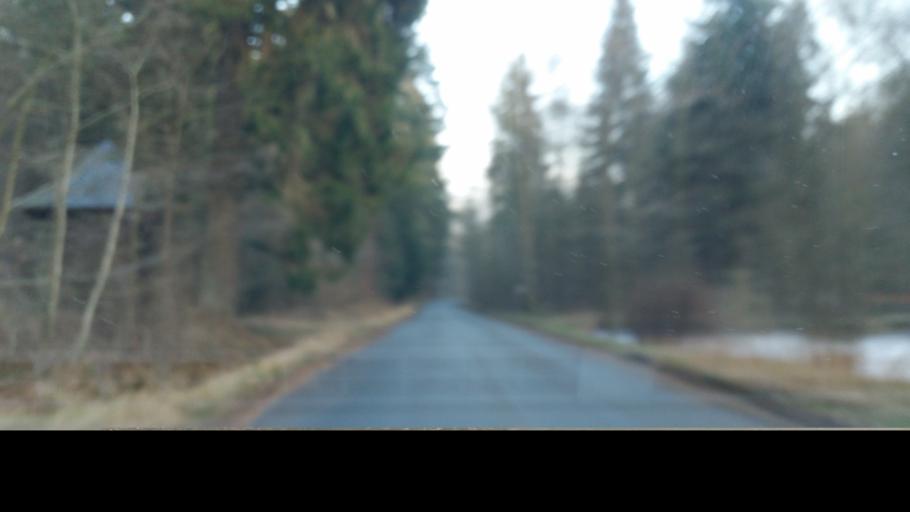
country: DE
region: Lower Saxony
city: Hameln
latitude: 52.0928
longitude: 9.3140
